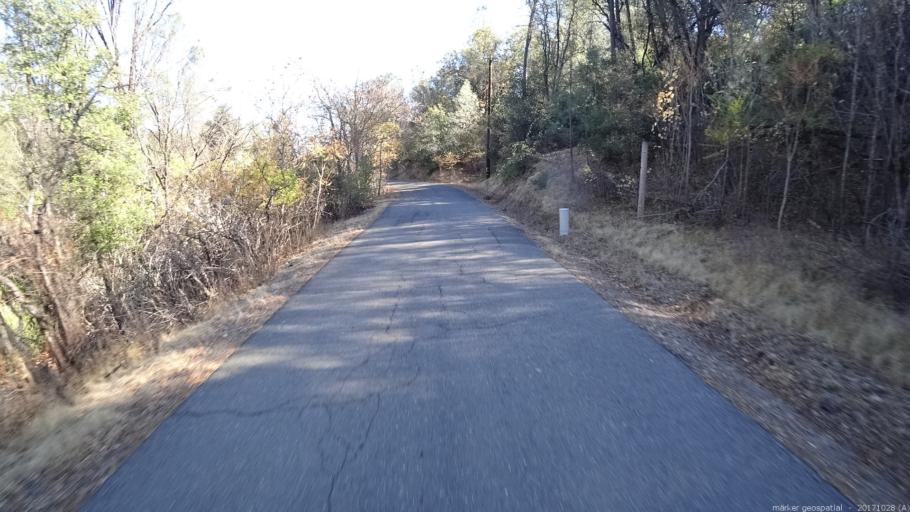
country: US
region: California
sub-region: Shasta County
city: Shasta
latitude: 40.5959
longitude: -122.4482
